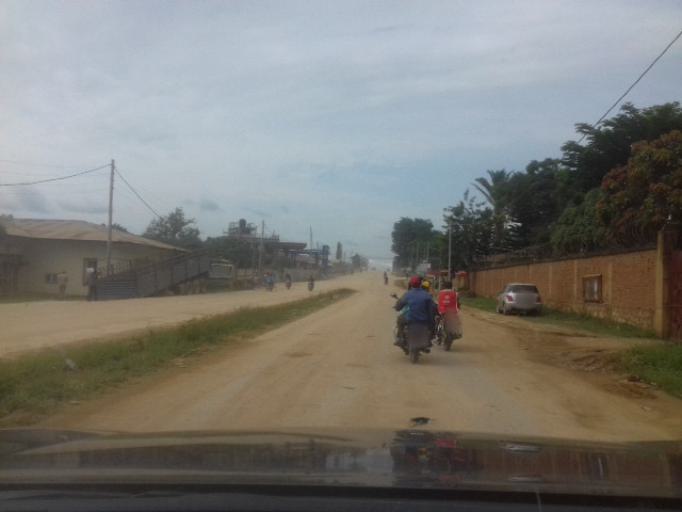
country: CD
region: Eastern Province
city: Bunia
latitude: 1.5511
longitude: 30.2486
